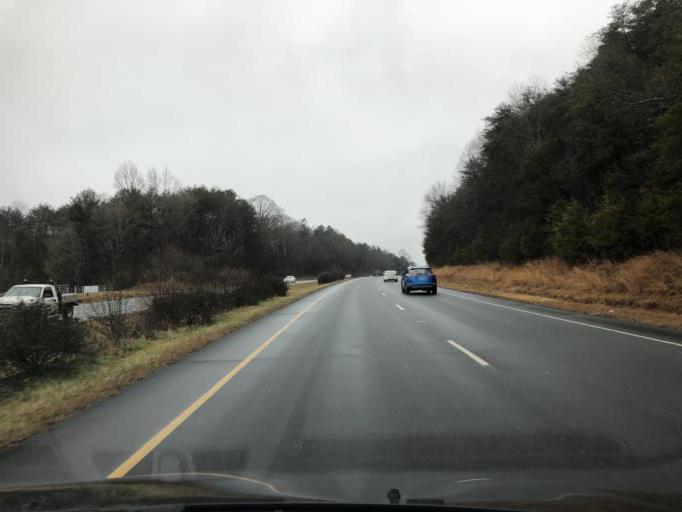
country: US
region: North Carolina
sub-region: Rutherford County
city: Spindale
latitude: 35.3493
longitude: -81.9382
